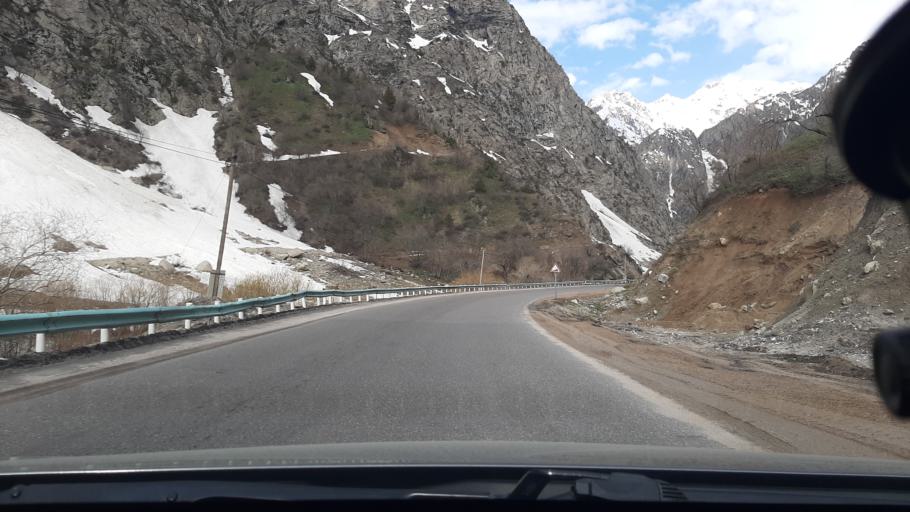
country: TJ
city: Tagob
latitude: 38.9631
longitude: 68.7722
